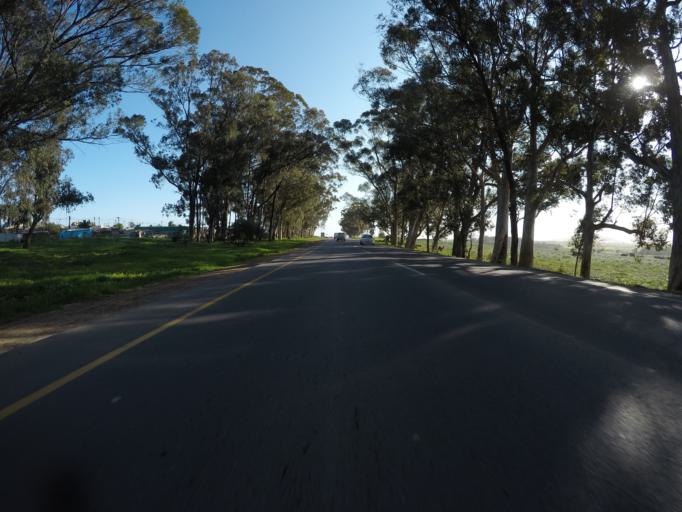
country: ZA
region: Western Cape
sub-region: City of Cape Town
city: Kraaifontein
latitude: -33.7800
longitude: 18.7176
